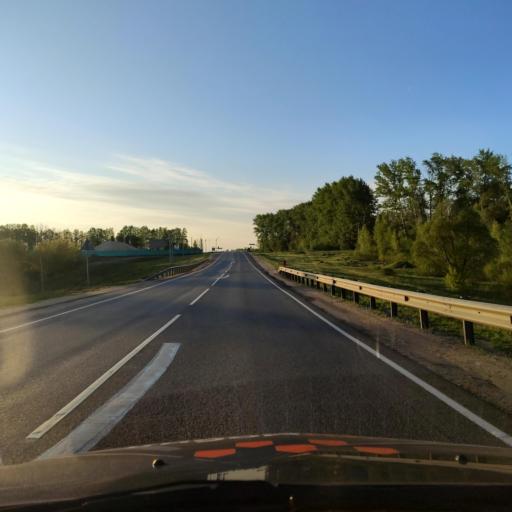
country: RU
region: Orjol
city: Livny
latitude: 52.4431
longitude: 37.5391
